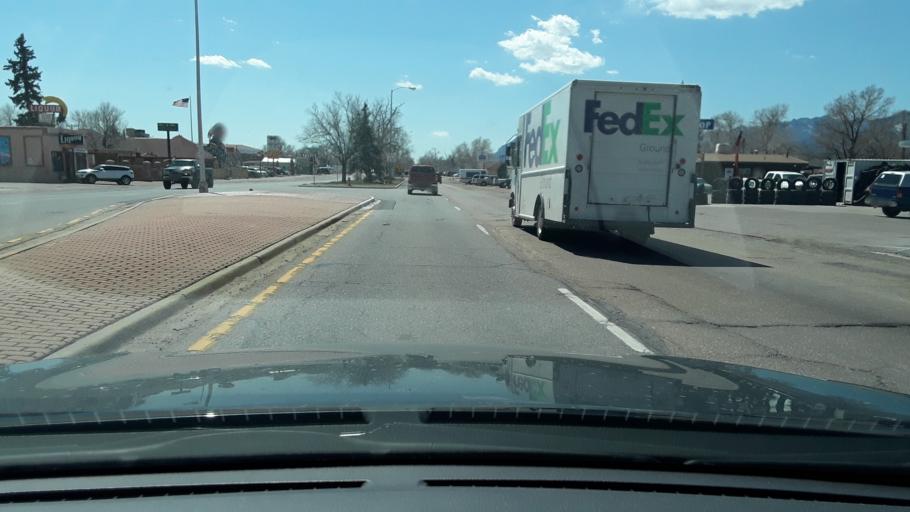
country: US
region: Colorado
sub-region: El Paso County
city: Colorado Springs
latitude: 38.8737
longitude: -104.8197
